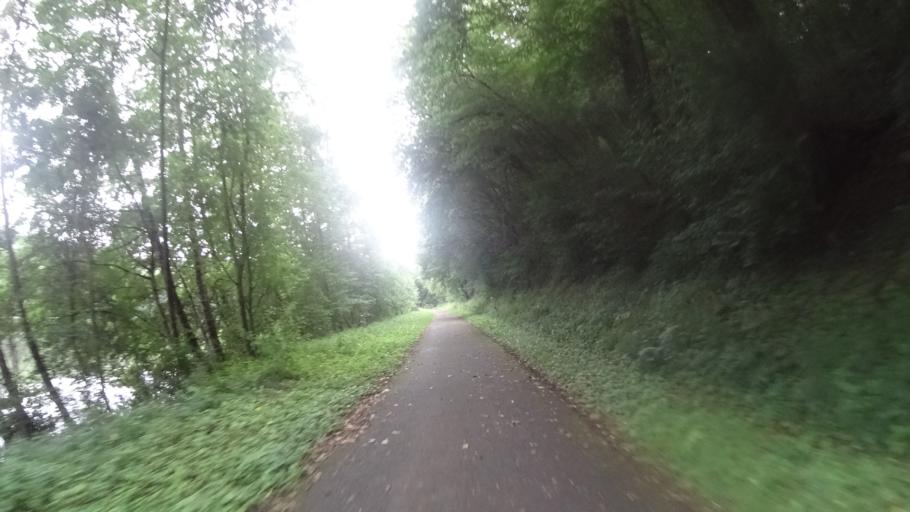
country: FR
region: Lorraine
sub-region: Departement de Meurthe-et-Moselle
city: Velaine-en-Haye
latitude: 48.6579
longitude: 6.0235
